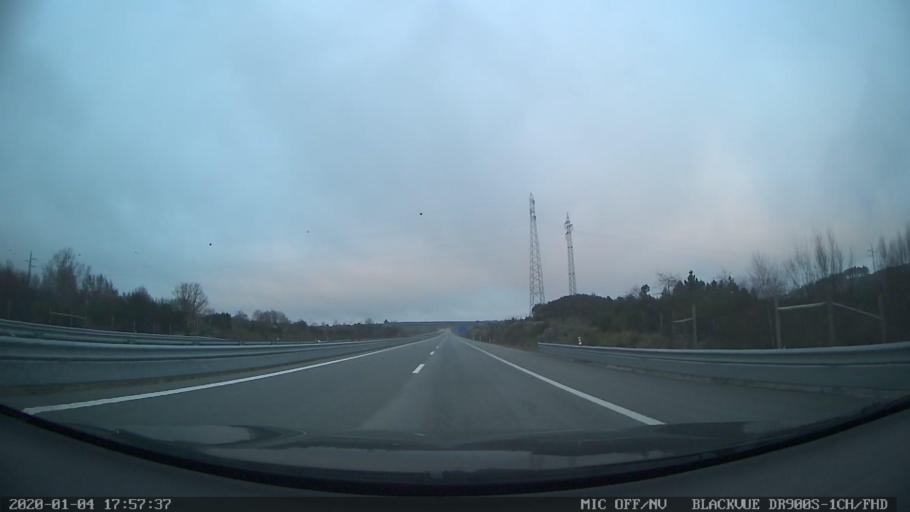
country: PT
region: Vila Real
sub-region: Vila Pouca de Aguiar
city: Vila Pouca de Aguiar
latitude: 41.4914
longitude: -7.6840
